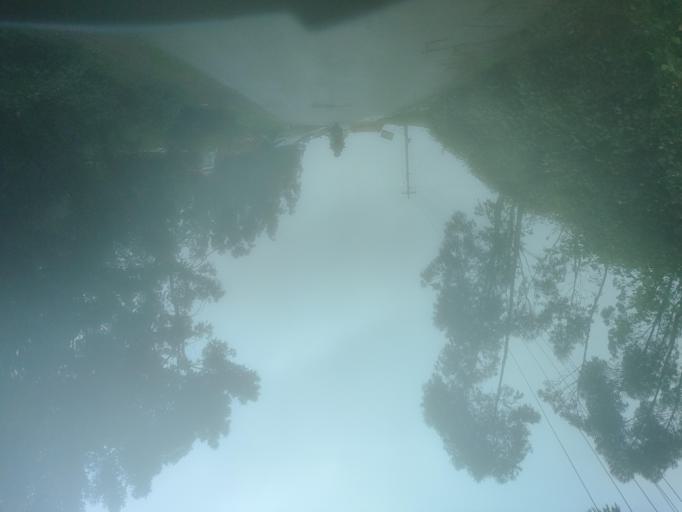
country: IN
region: Tamil Nadu
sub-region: Dindigul
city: Kodaikanal
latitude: 10.2047
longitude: 77.3444
